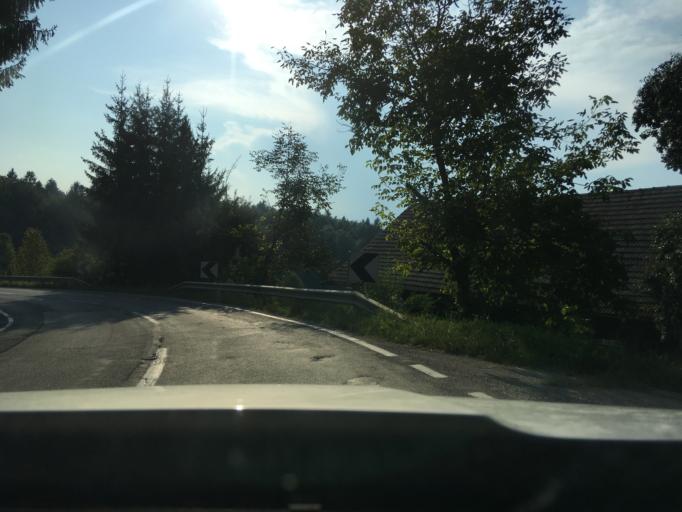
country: SI
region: Novo Mesto
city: Novo Mesto
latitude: 45.7723
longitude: 15.1905
